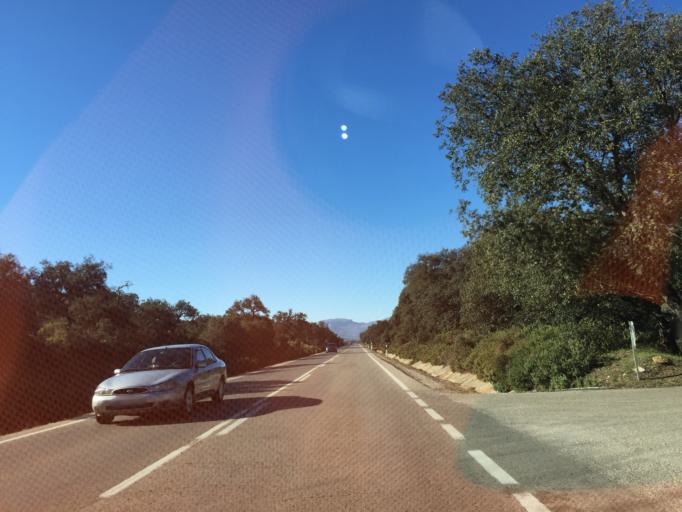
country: ES
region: Andalusia
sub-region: Provincia de Malaga
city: Arriate
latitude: 36.8222
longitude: -5.0963
